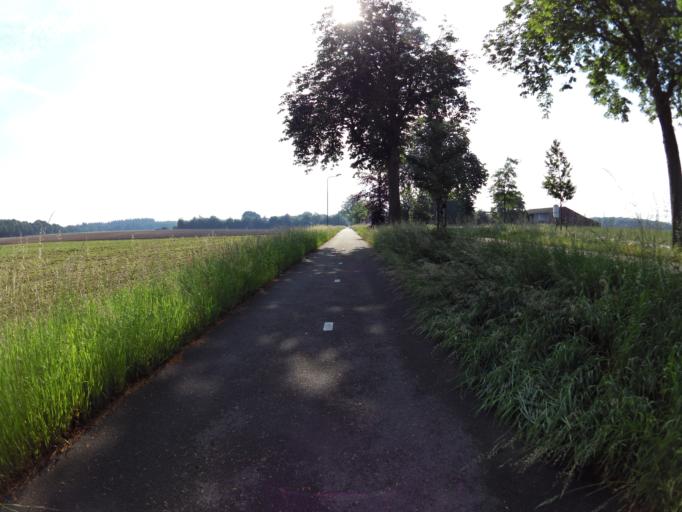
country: NL
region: Limburg
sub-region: Gemeente Echt-Susteren
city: Koningsbosch
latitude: 51.0835
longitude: 5.9367
